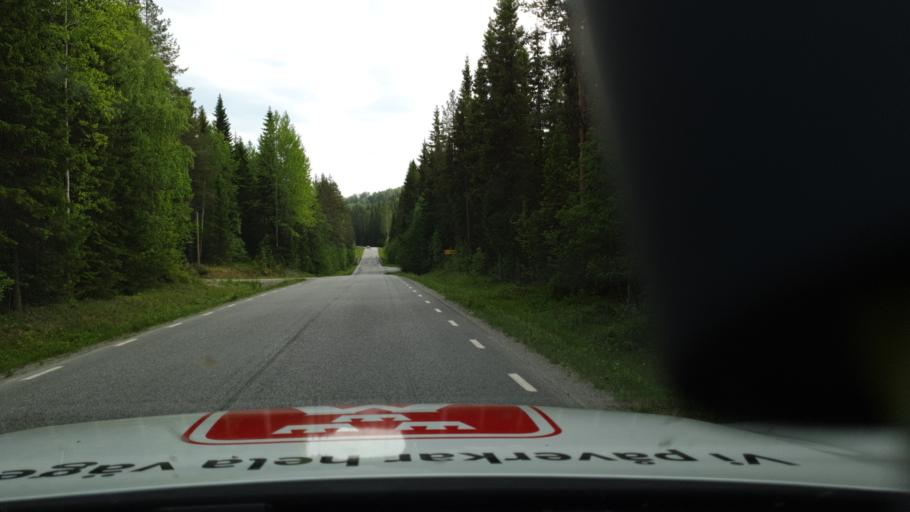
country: SE
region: Jaemtland
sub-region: Braecke Kommun
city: Braecke
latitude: 62.9986
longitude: 15.1976
